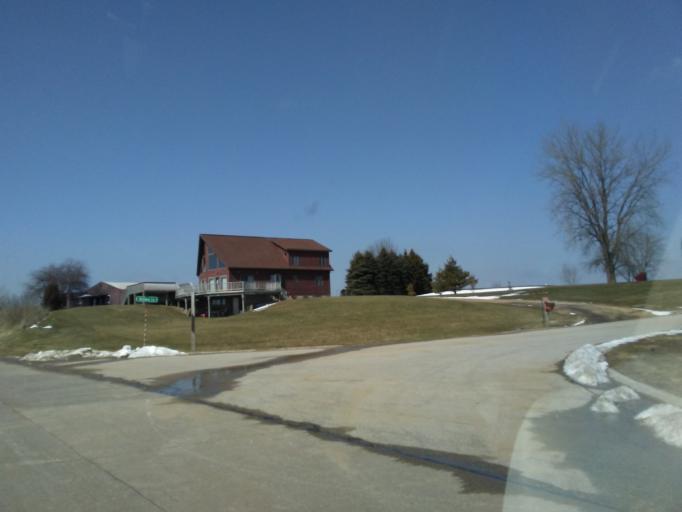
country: US
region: Wisconsin
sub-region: La Crosse County
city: West Salem
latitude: 43.7137
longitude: -91.0685
